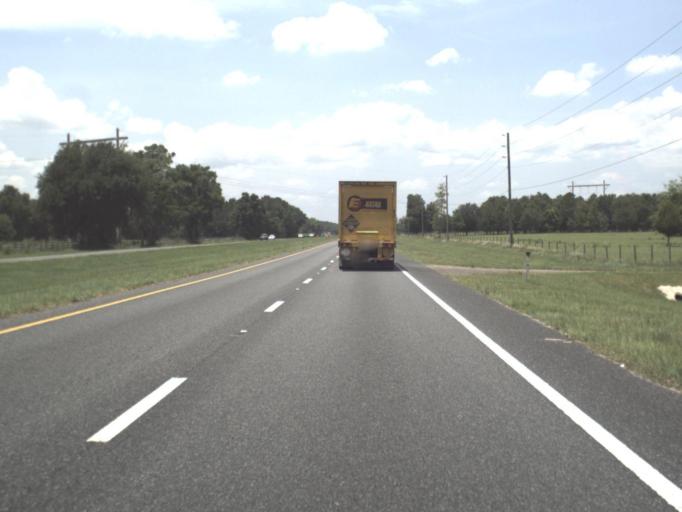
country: US
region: Florida
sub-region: Alachua County
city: Newberry
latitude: 29.6548
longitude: -82.5649
